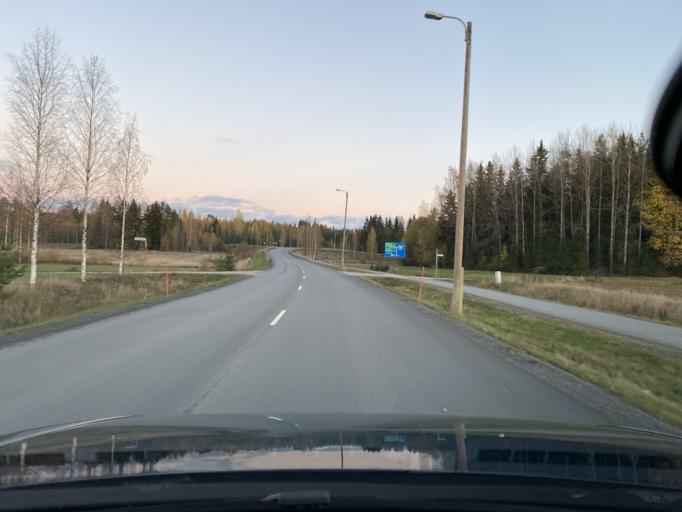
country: FI
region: Pirkanmaa
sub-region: Tampere
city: Lempaeaelae
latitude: 61.3273
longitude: 23.7700
